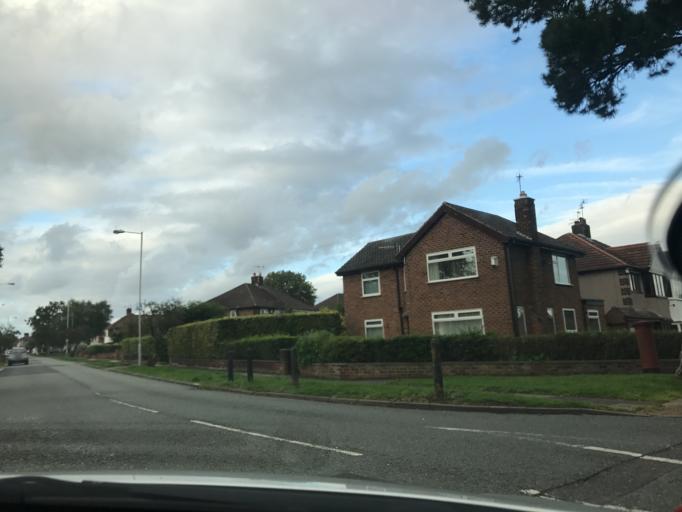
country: GB
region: England
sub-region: Metropolitan Borough of Wirral
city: Bebington
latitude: 53.3413
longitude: -3.0107
